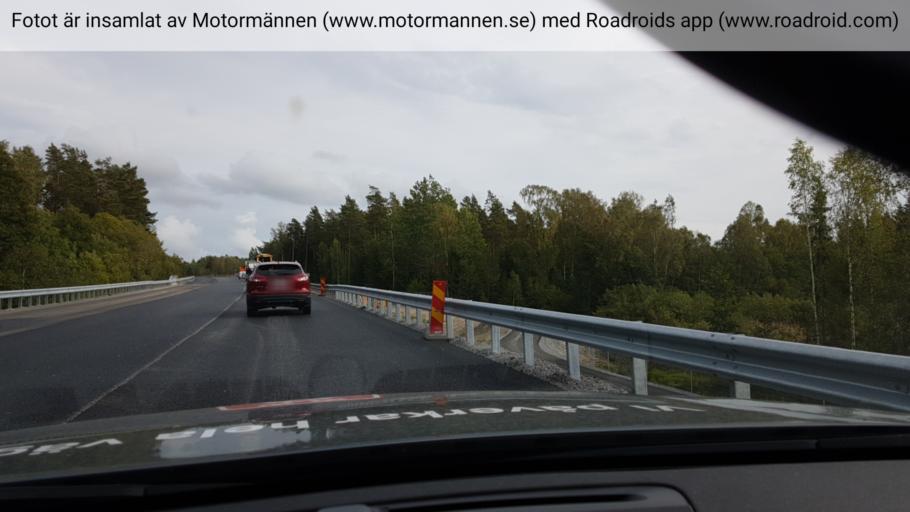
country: SE
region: Stockholm
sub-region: Norrtalje Kommun
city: Bjorko
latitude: 59.7196
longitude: 18.9220
